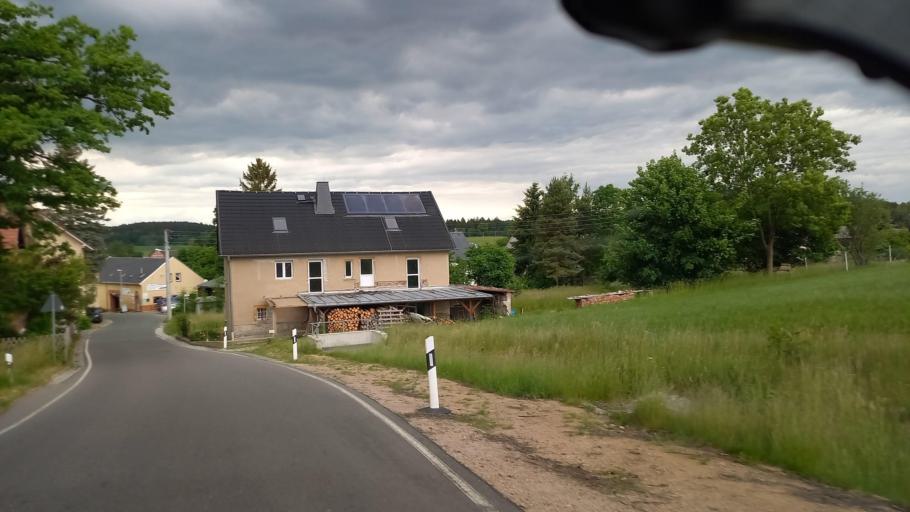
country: DE
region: Saxony
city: Rodewisch
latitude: 50.5535
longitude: 12.4579
